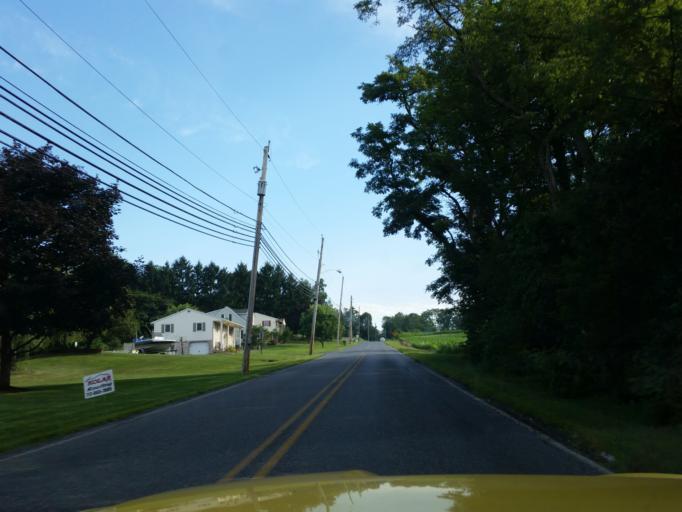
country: US
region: Pennsylvania
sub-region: Lebanon County
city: Jonestown
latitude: 40.4168
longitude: -76.4704
